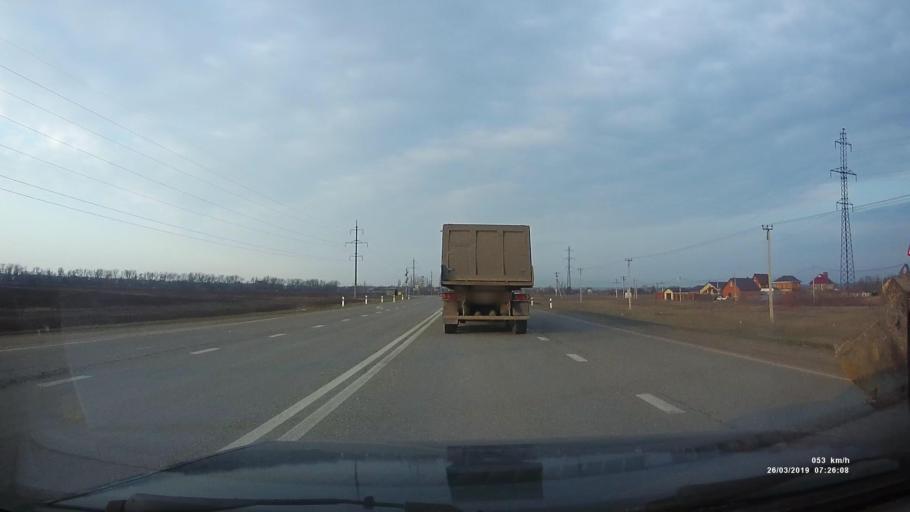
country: RU
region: Rostov
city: Taganrog
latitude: 47.2687
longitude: 38.8435
